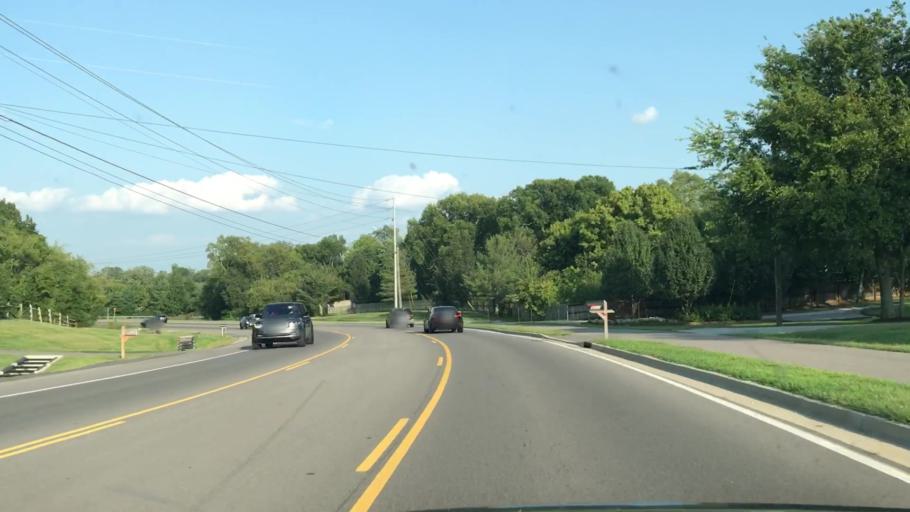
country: US
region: Tennessee
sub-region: Williamson County
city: Nolensville
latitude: 35.9831
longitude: -86.7199
